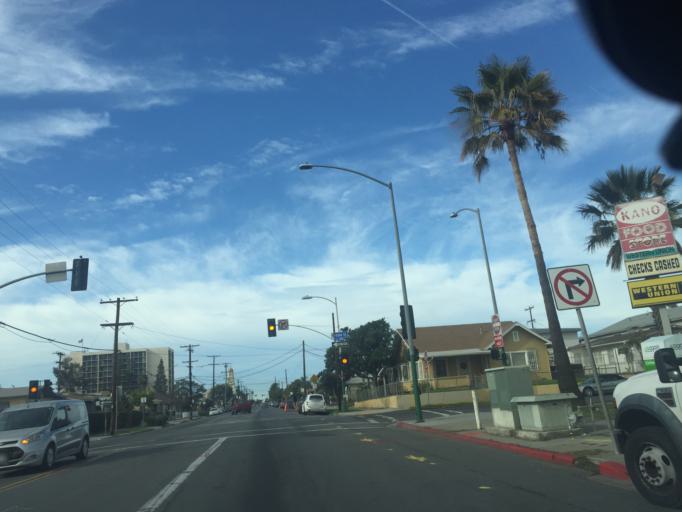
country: US
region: California
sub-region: San Diego County
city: San Diego
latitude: 32.7533
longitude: -117.1018
